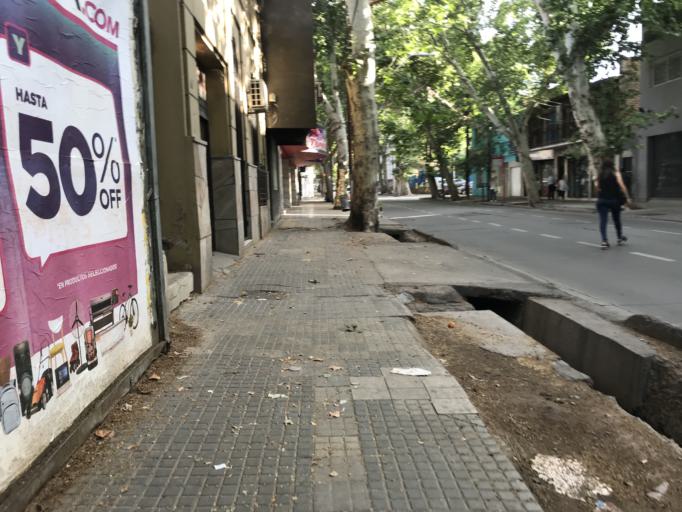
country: AR
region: Mendoza
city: Mendoza
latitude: -32.8854
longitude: -68.8354
